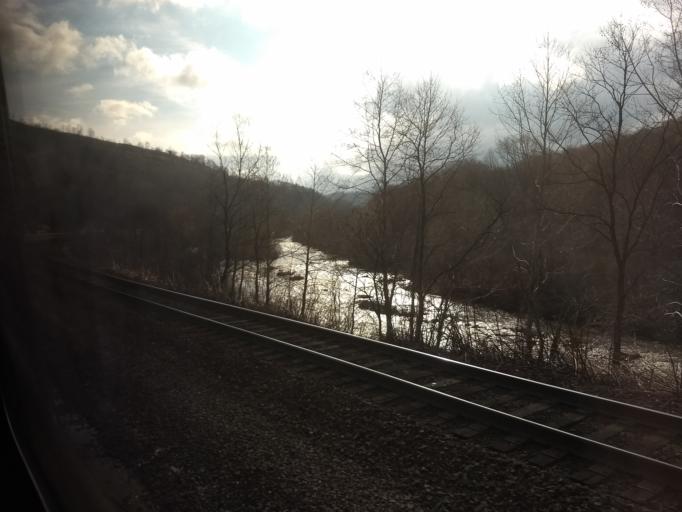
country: US
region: Pennsylvania
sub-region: Cambria County
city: Vinco
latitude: 40.3694
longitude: -78.8124
